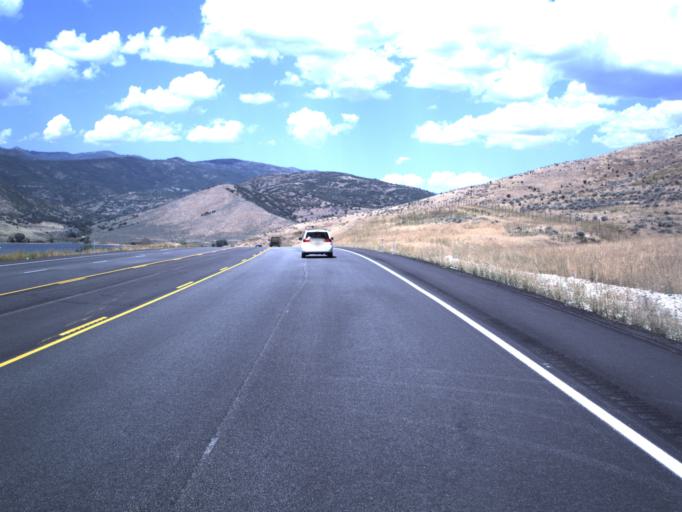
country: US
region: Utah
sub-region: Wasatch County
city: Midway
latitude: 40.4303
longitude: -111.4902
